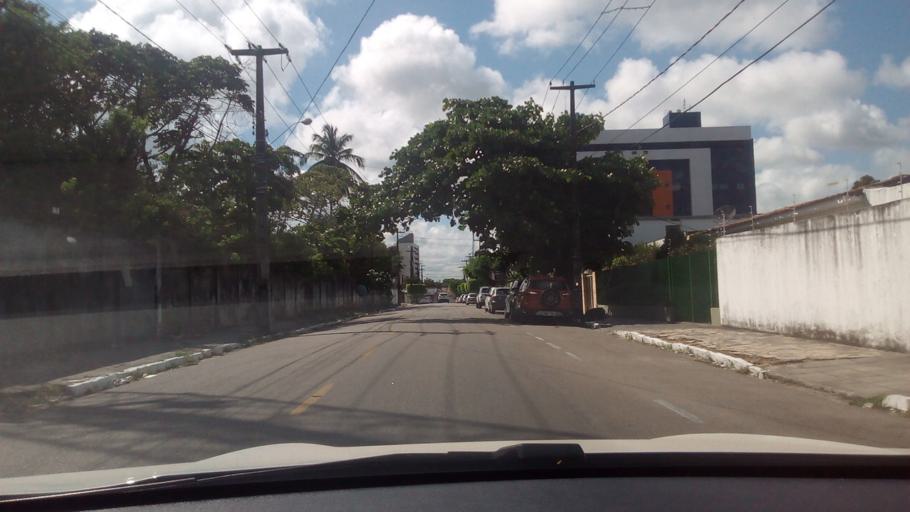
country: BR
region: Paraiba
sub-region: Joao Pessoa
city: Joao Pessoa
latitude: -7.1273
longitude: -34.8693
